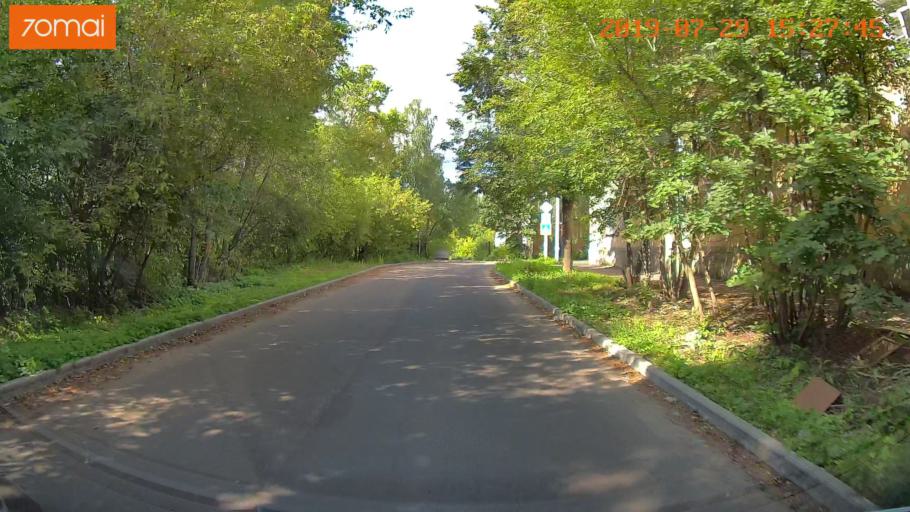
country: RU
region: Ivanovo
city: Bogorodskoye
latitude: 57.0246
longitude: 41.0104
